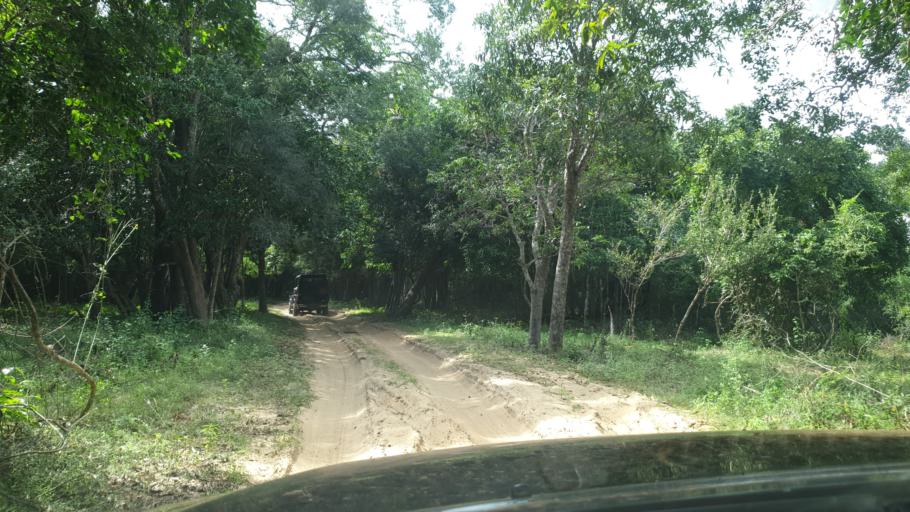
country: LK
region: North Western
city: Puttalam
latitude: 8.4121
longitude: 79.9876
